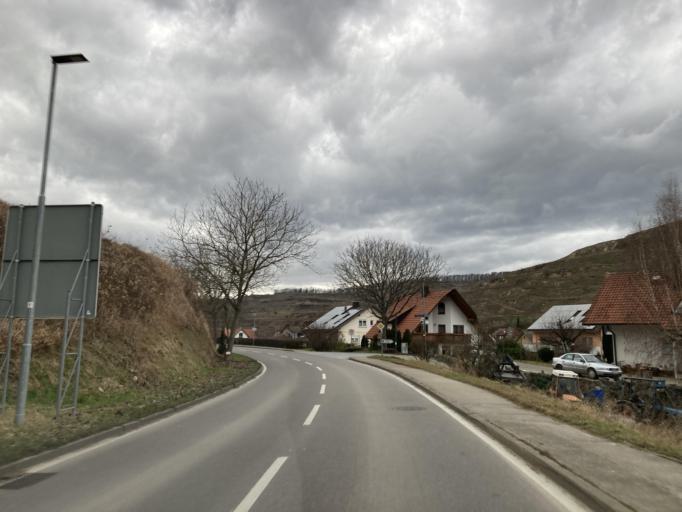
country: DE
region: Baden-Wuerttemberg
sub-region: Freiburg Region
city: Vogtsburg
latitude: 48.0964
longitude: 7.6622
